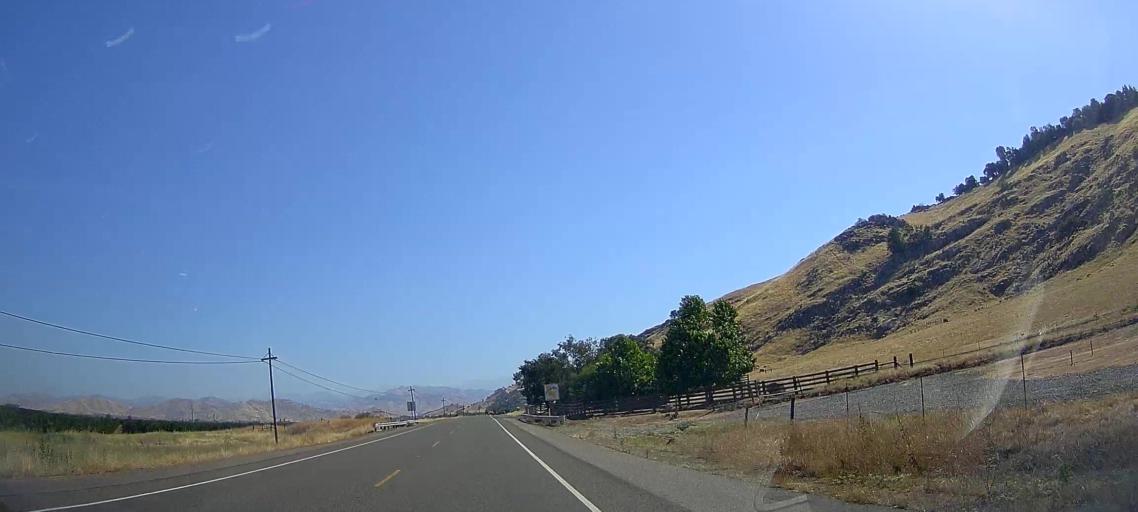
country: US
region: California
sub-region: Tulare County
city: Exeter
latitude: 36.3361
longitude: -119.0702
